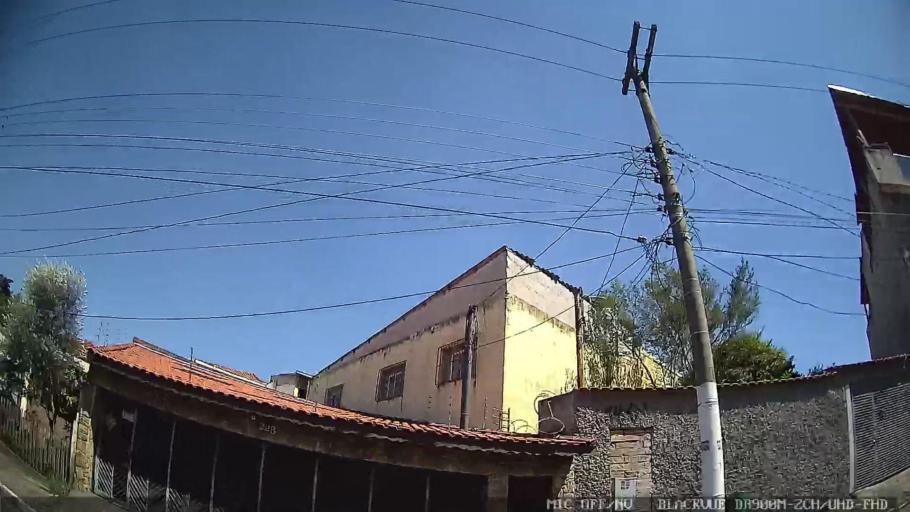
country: BR
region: Sao Paulo
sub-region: Sao Caetano Do Sul
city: Sao Caetano do Sul
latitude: -23.5842
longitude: -46.4984
